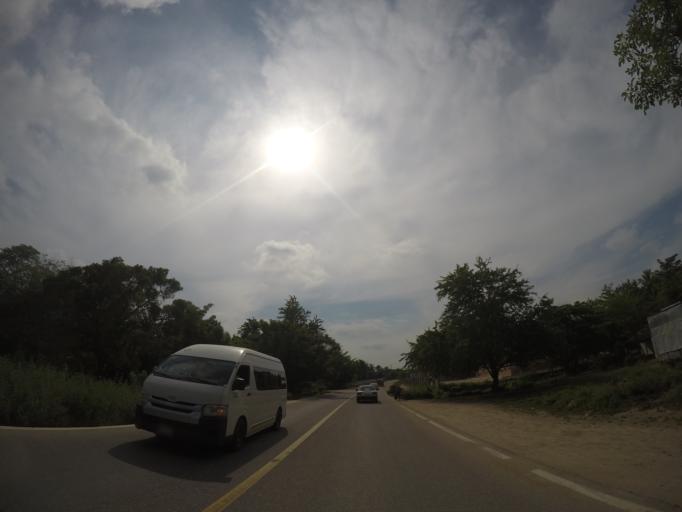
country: MX
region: Guerrero
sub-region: Acapulco de Juarez
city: Cerro de Piedra
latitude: 16.7751
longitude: -99.6280
